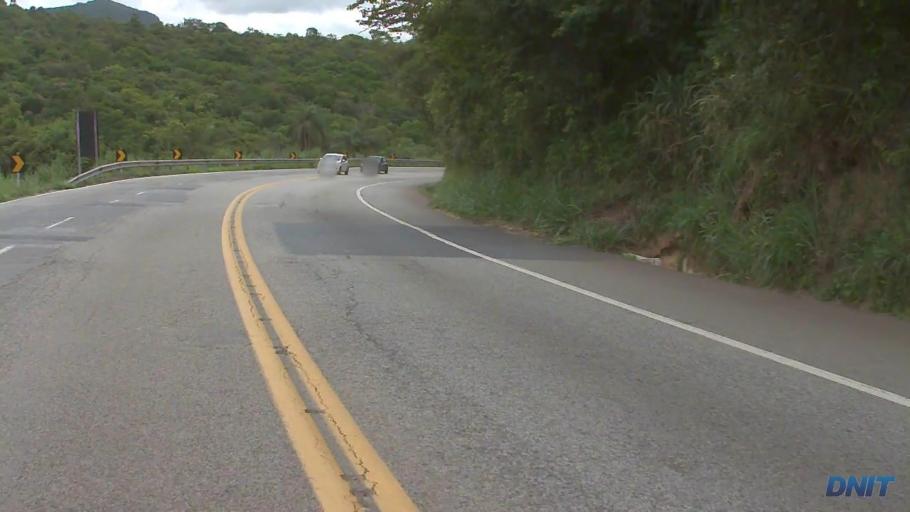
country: BR
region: Minas Gerais
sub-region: Barao De Cocais
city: Barao de Cocais
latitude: -19.8360
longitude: -43.3495
